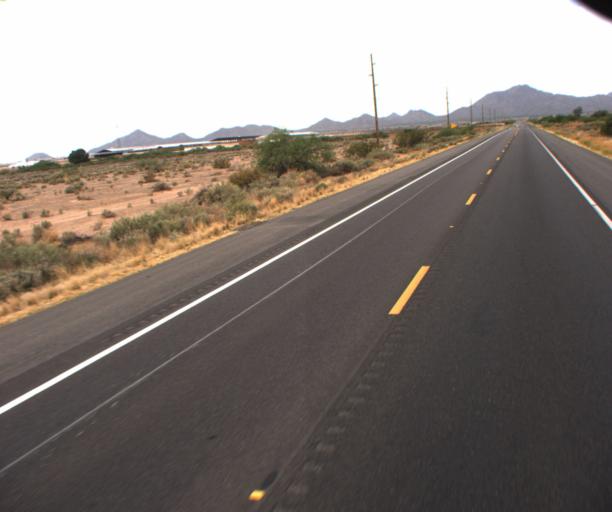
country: US
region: Arizona
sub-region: Pinal County
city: Blackwater
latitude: 33.0025
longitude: -111.5881
